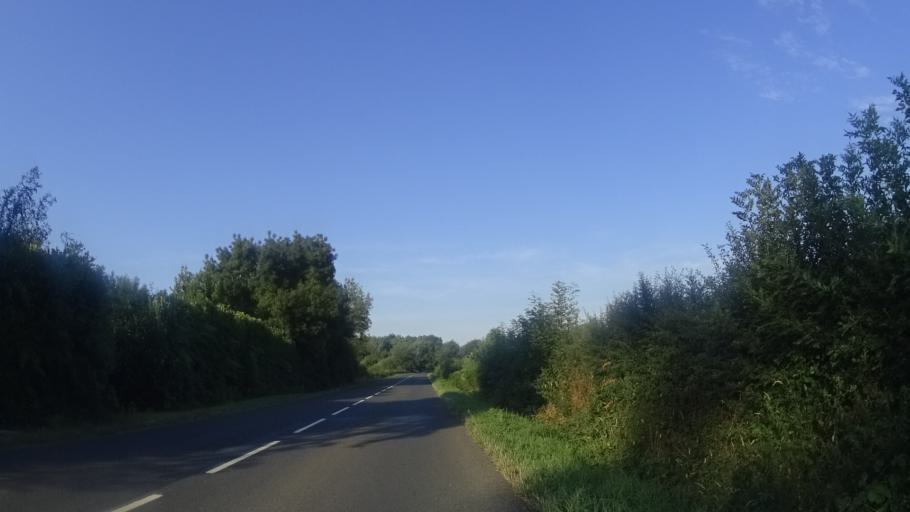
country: FR
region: Pays de la Loire
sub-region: Departement de la Loire-Atlantique
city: Riaille
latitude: 47.5164
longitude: -1.2751
